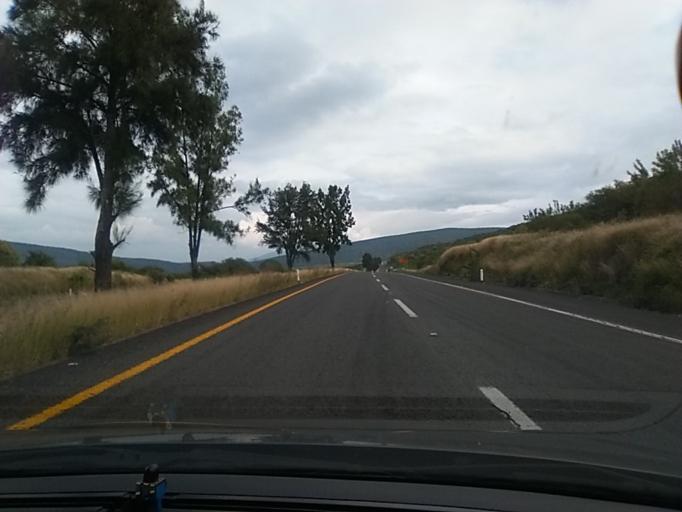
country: MX
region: Michoacan
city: Ixtlan
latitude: 20.2282
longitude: -102.3741
